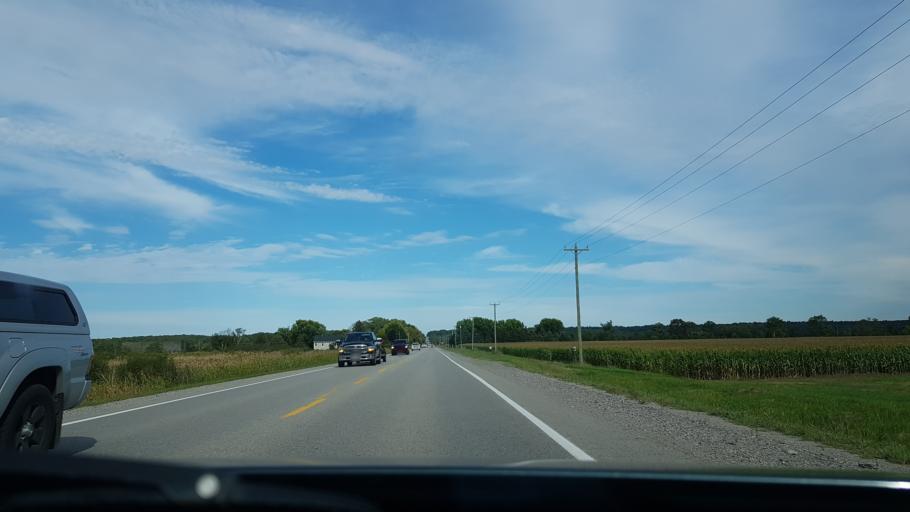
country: CA
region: Ontario
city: Angus
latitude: 44.4718
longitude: -79.8533
